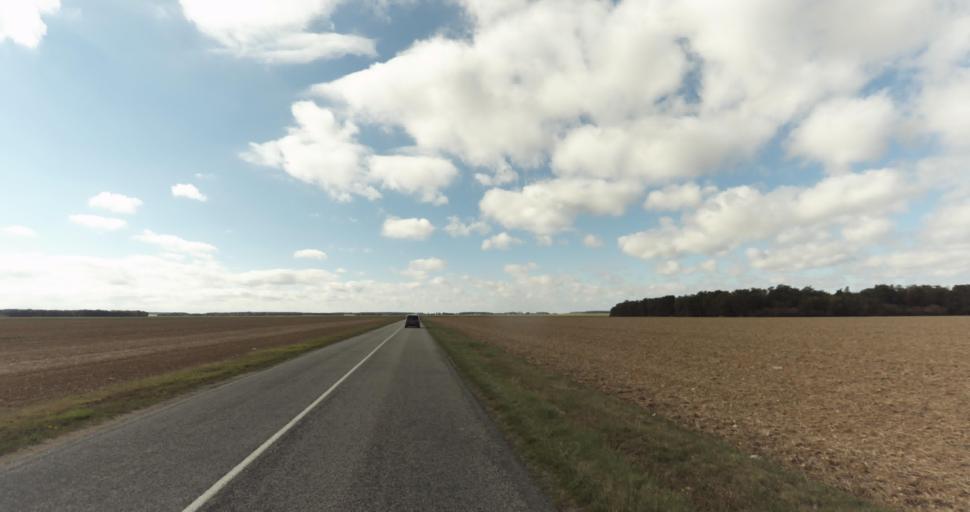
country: FR
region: Centre
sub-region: Departement d'Eure-et-Loir
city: Garnay
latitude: 48.7164
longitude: 1.3161
